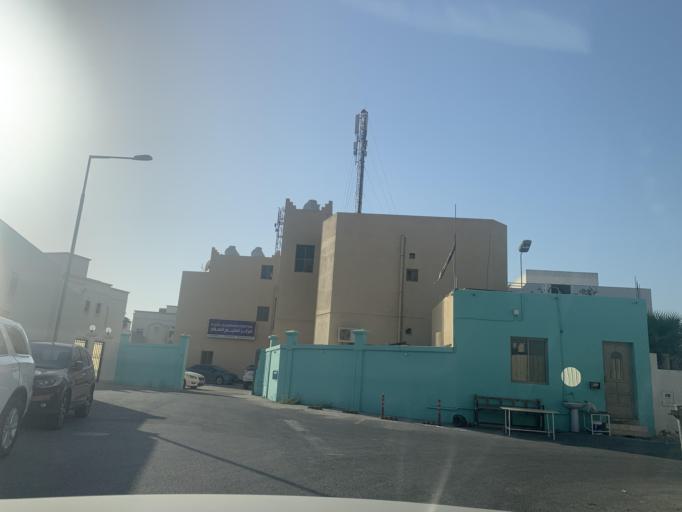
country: BH
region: Manama
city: Jidd Hafs
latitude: 26.1980
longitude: 50.4817
